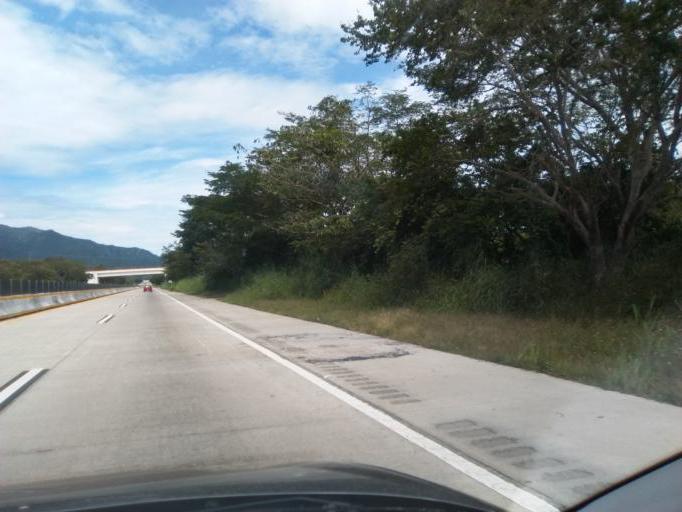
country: MX
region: Guerrero
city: El Ocotito
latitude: 17.2498
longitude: -99.5204
